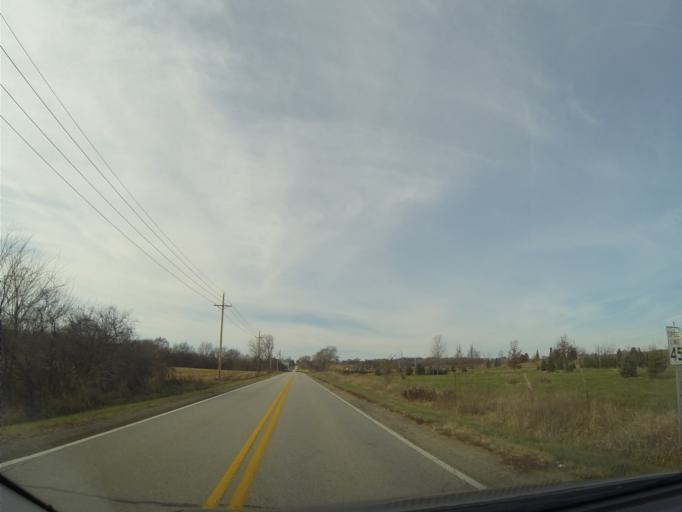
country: US
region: Nebraska
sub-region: Douglas County
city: Elkhorn
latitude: 41.2776
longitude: -96.1982
